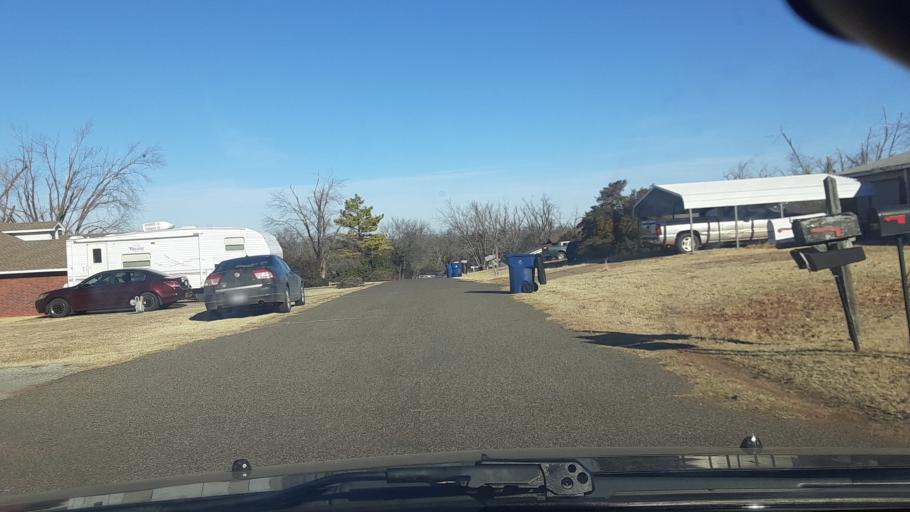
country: US
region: Oklahoma
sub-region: Logan County
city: Guthrie
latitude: 35.8572
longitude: -97.4311
